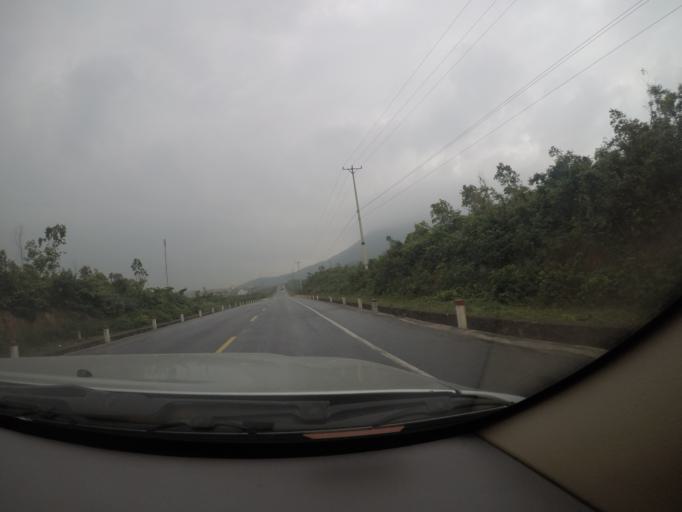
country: VN
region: Ha Tinh
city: Ky Anh
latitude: 18.0003
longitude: 106.4477
